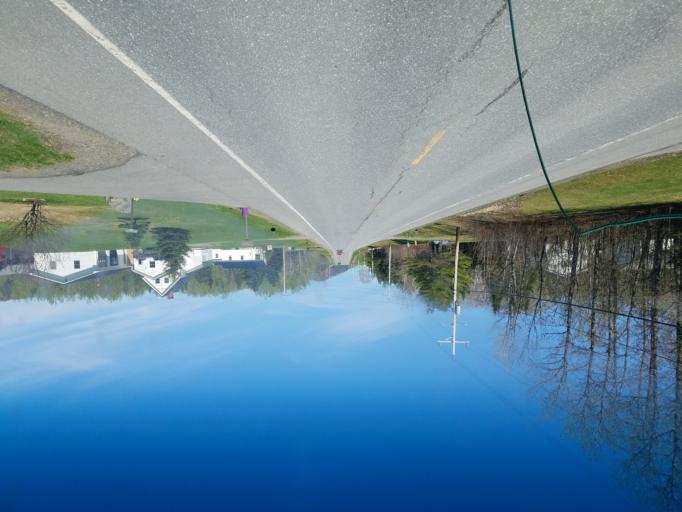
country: US
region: Maine
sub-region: Aroostook County
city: Presque Isle
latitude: 46.6668
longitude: -68.2054
